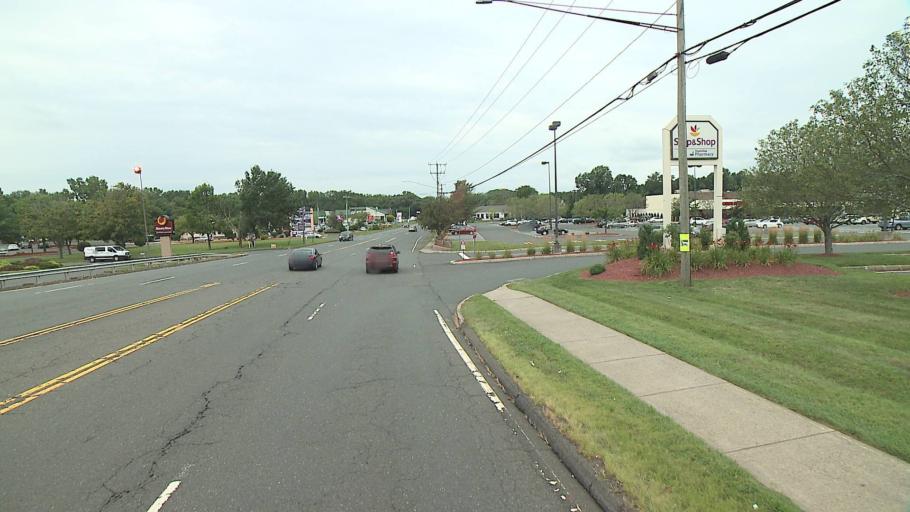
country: US
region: Connecticut
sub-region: Middlesex County
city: Cromwell
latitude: 41.6029
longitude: -72.6762
